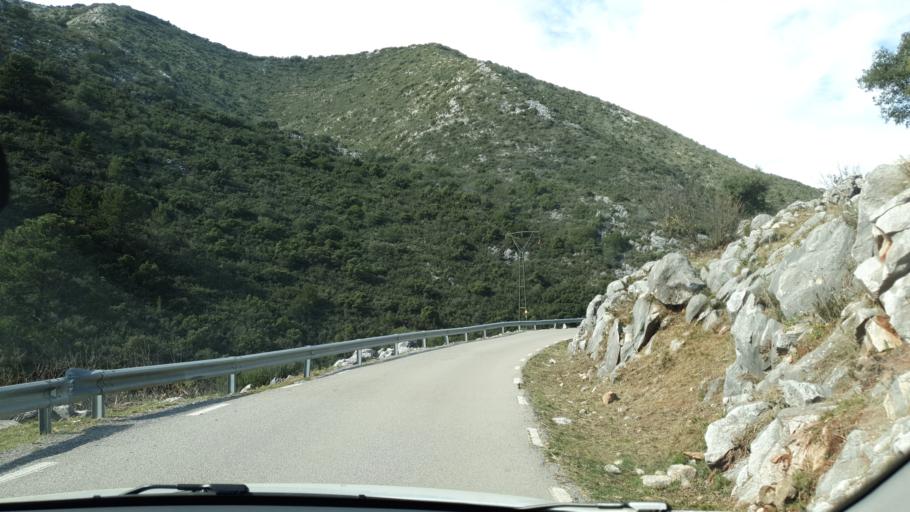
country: ES
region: Andalusia
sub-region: Provincia de Malaga
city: Ojen
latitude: 36.5823
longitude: -4.8841
